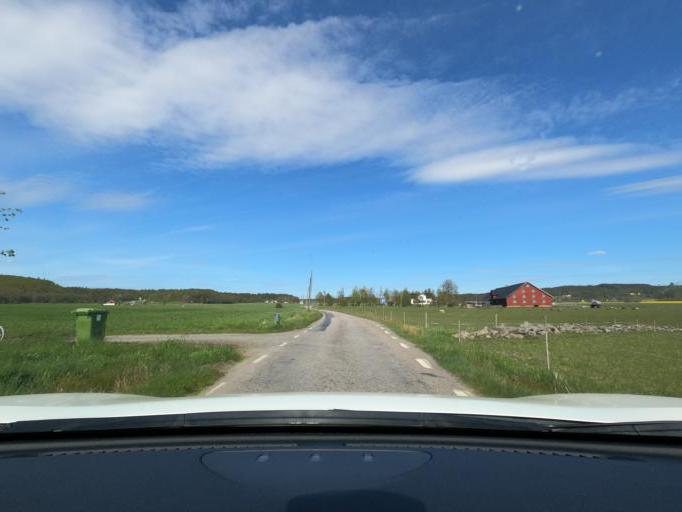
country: SE
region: Vaestra Goetaland
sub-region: Marks Kommun
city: Horred
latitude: 57.4523
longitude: 12.4840
